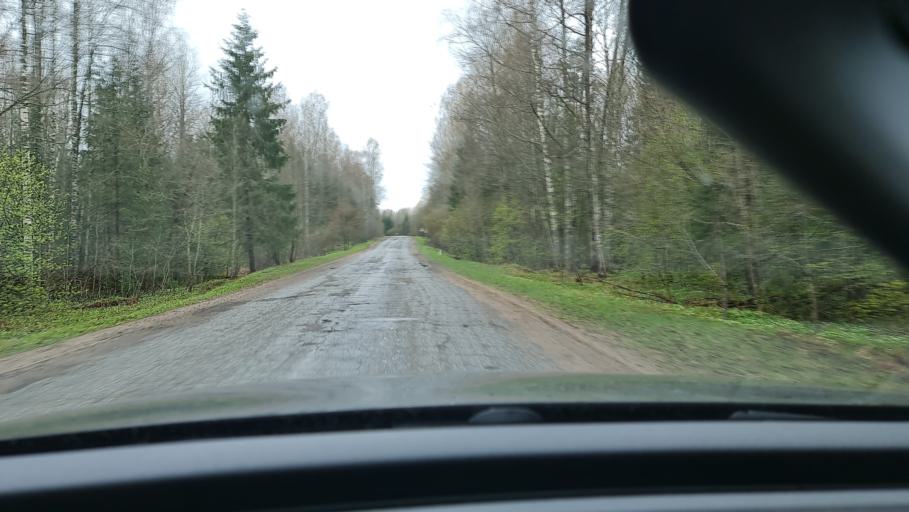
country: RU
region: Novgorod
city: Marevo
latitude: 57.2637
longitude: 32.0734
